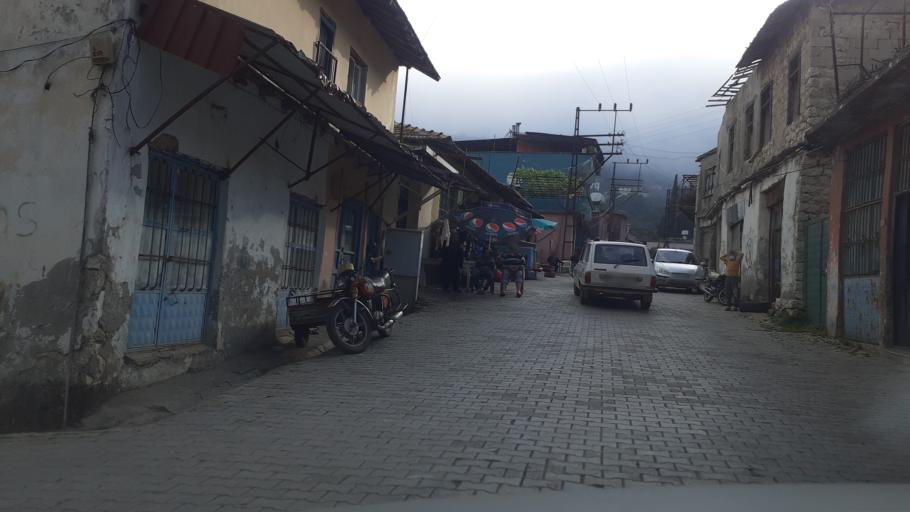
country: TR
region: Hatay
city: Yeditepe
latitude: 35.9682
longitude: 36.0140
